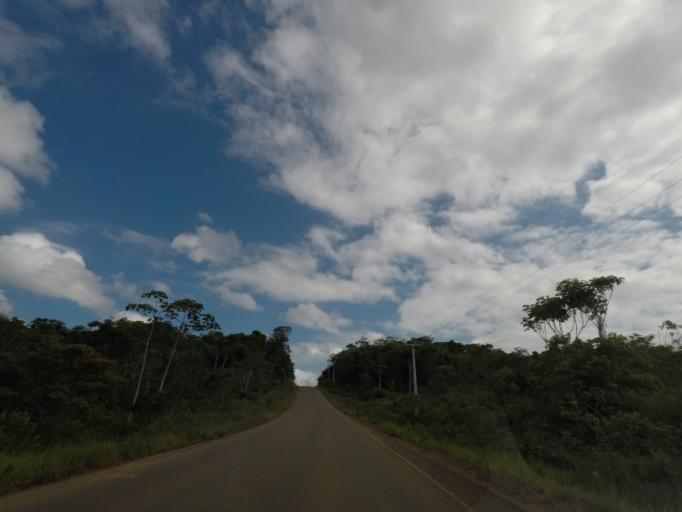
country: BR
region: Bahia
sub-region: Itacare
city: Itacare
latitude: -14.2170
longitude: -39.1001
